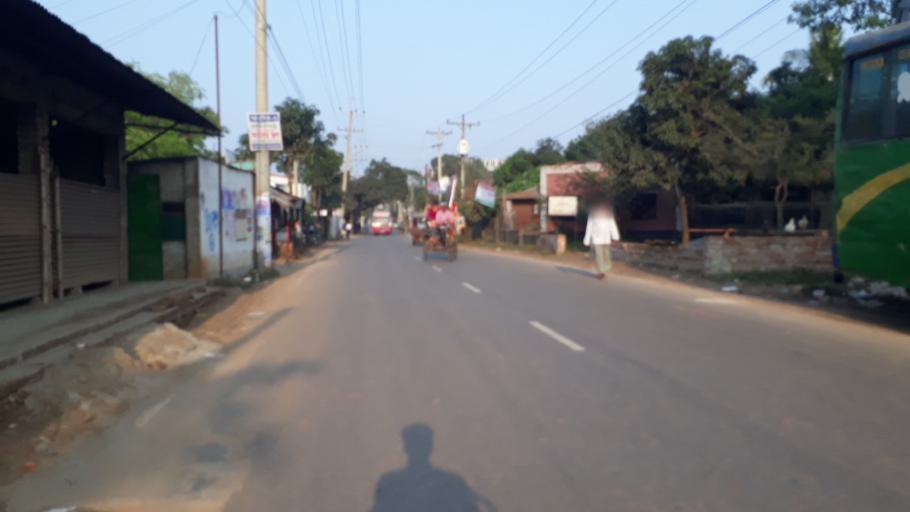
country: BD
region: Dhaka
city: Tungi
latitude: 23.8761
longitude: 90.2882
